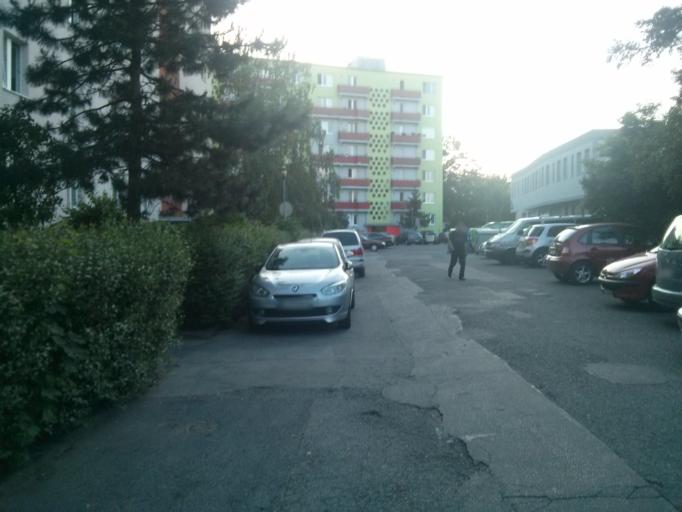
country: SK
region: Bratislavsky
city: Bratislava
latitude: 48.1727
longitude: 17.1324
